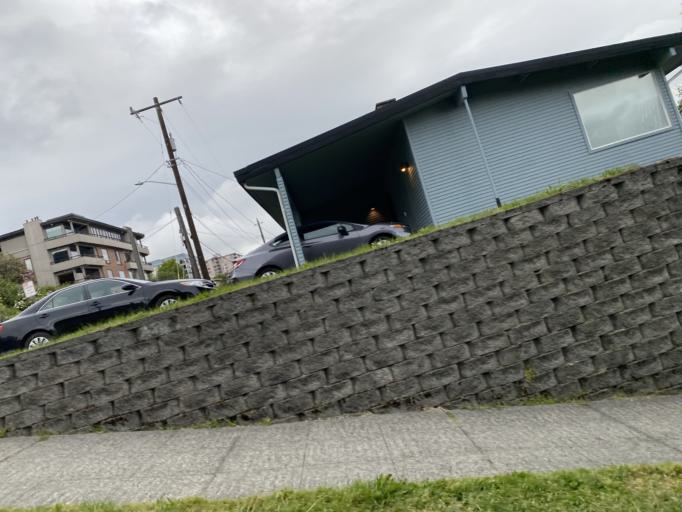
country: US
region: Washington
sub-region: King County
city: Seattle
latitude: 47.6278
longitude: -122.3605
